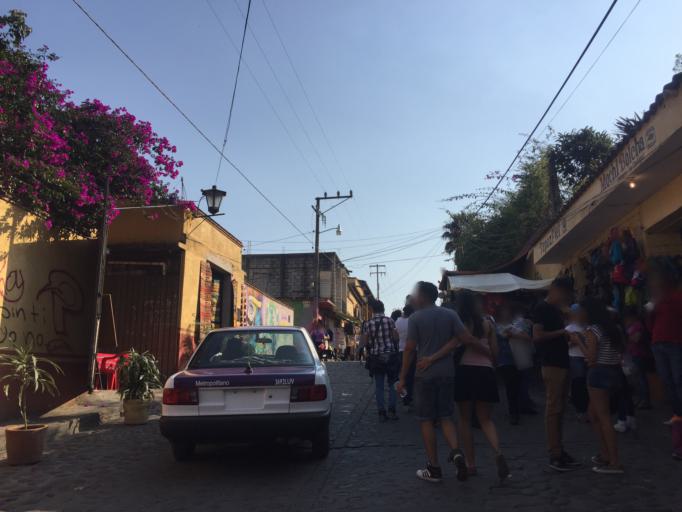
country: MX
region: Morelos
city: Tepoztlan
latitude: 18.9902
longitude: -99.1006
